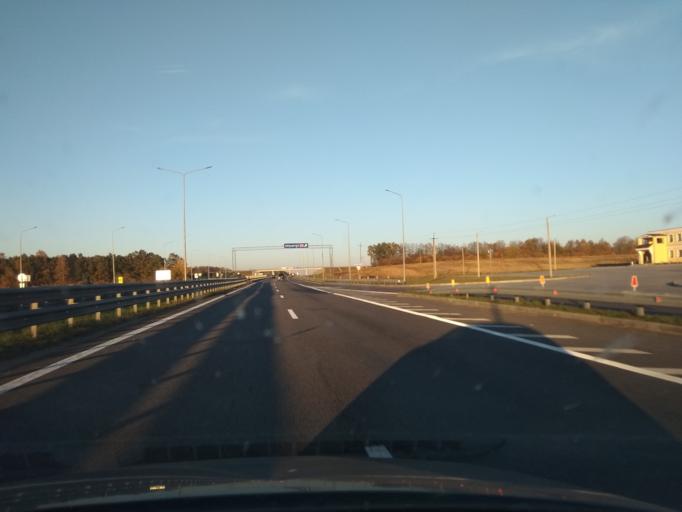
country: BY
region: Brest
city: Baranovichi
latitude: 53.1919
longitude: 26.0765
